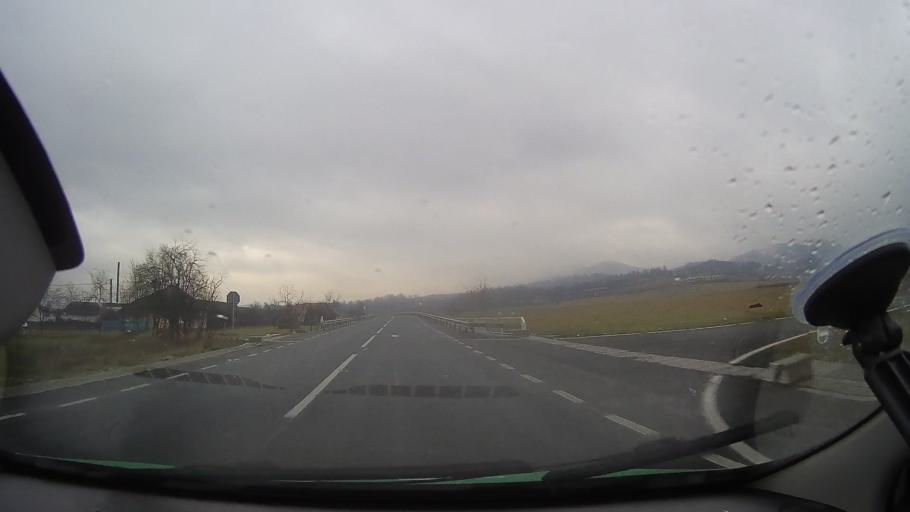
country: RO
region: Hunedoara
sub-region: Comuna Baia de Cris
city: Baia de Cris
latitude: 46.1757
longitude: 22.7081
